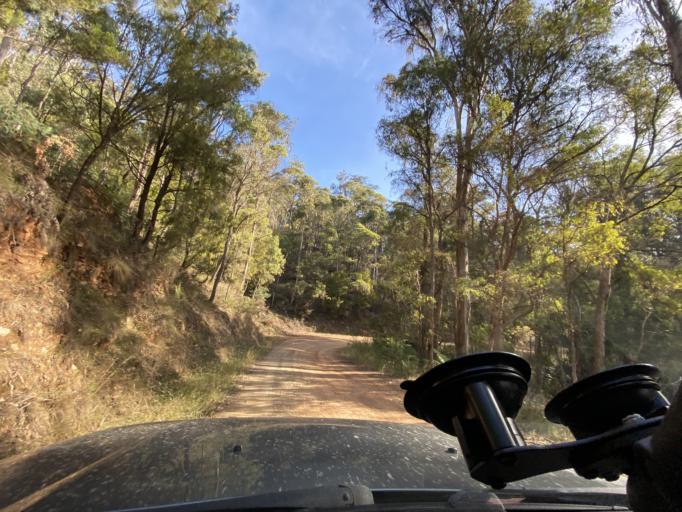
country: AU
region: Victoria
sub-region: Mansfield
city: Mansfield
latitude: -37.5220
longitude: 146.0797
